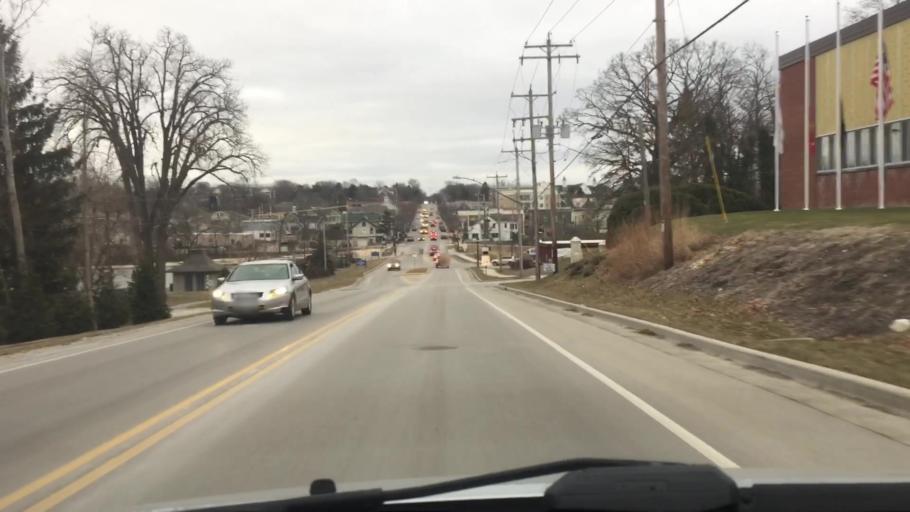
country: US
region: Wisconsin
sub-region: Waukesha County
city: Delafield
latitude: 43.0647
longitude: -88.4041
